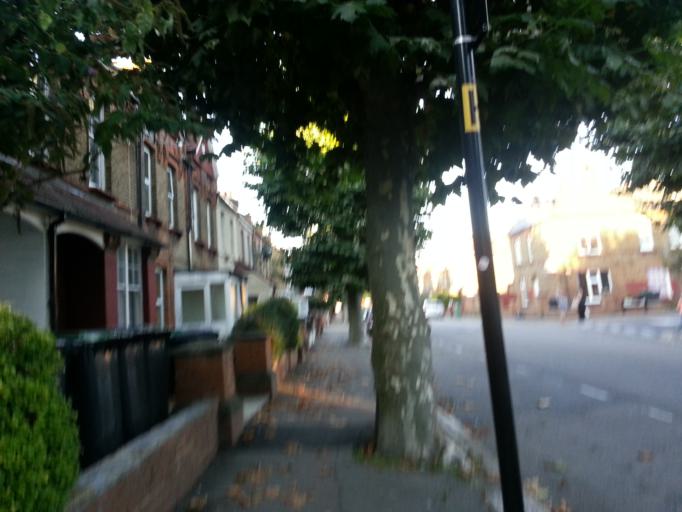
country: GB
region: England
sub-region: Greater London
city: Wood Green
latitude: 51.5986
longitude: -0.1009
